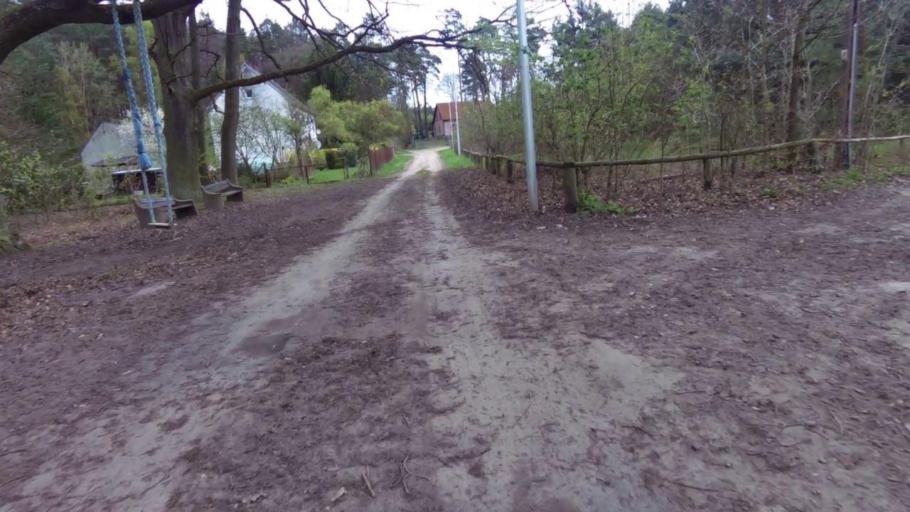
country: PL
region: West Pomeranian Voivodeship
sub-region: Powiat kamienski
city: Wolin
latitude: 53.9726
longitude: 14.5872
